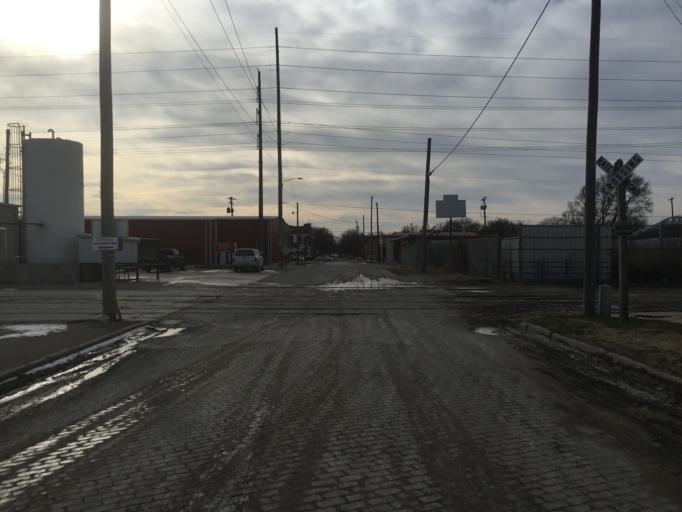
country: US
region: Kansas
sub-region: Sedgwick County
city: Wichita
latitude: 37.7171
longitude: -97.3335
